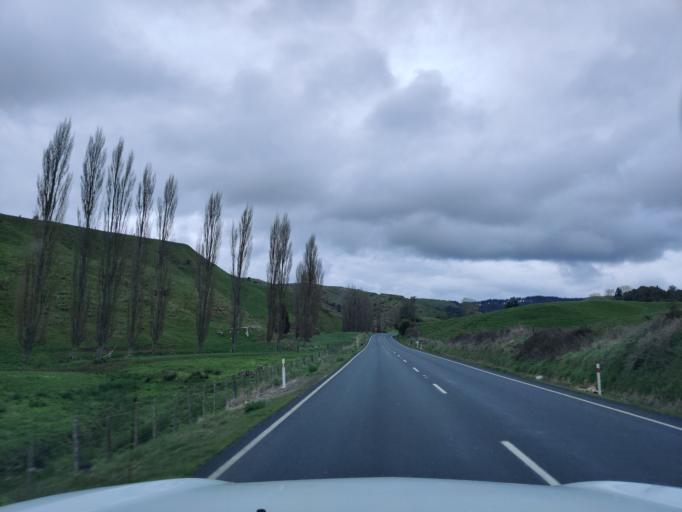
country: NZ
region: Waikato
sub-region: Otorohanga District
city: Otorohanga
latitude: -38.5197
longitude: 175.1891
